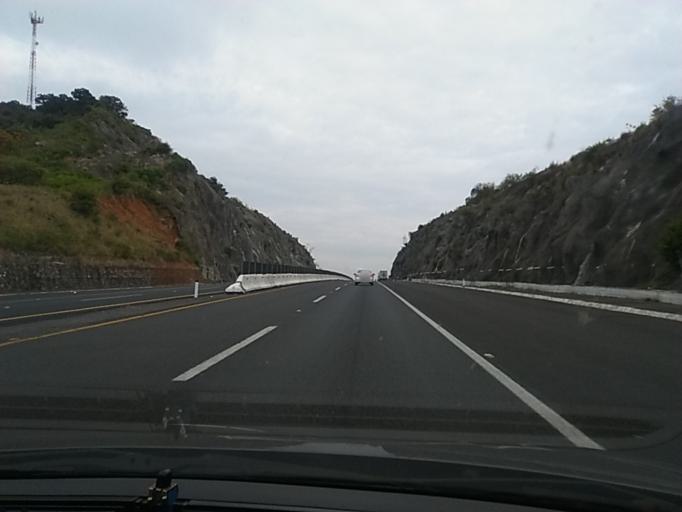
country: MX
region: Michoacan
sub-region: Puruandiro
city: San Lorenzo
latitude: 19.9424
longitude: -101.6298
